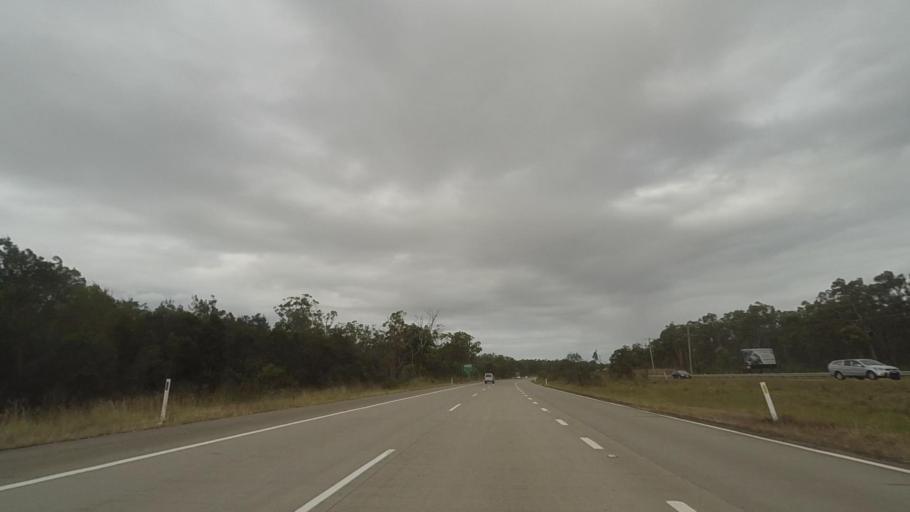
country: AU
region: New South Wales
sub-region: Port Stephens Shire
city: Port Stephens
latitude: -32.6128
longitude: 152.0808
